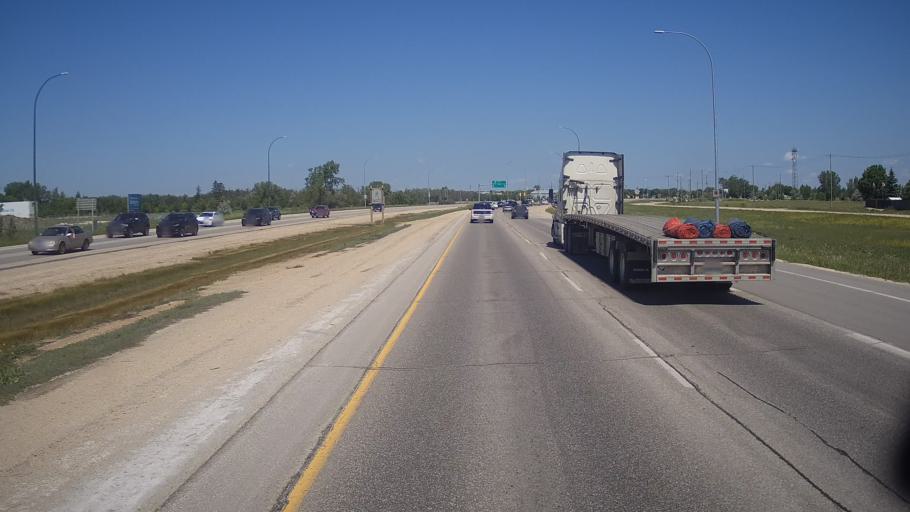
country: CA
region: Manitoba
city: Winnipeg
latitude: 49.9243
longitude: -97.0482
